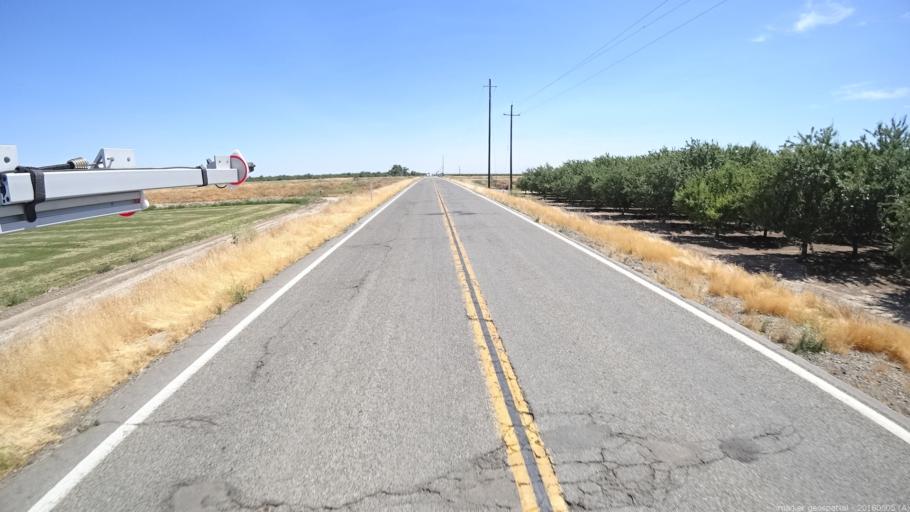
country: US
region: California
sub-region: Fresno County
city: Firebaugh
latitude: 36.9775
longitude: -120.3830
